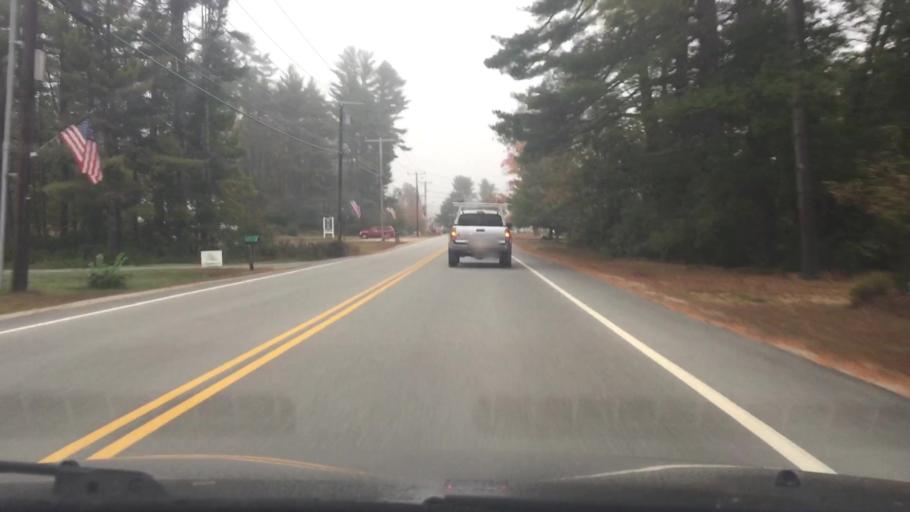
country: US
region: New Hampshire
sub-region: Cheshire County
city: Swanzey
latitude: 42.8708
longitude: -72.2822
